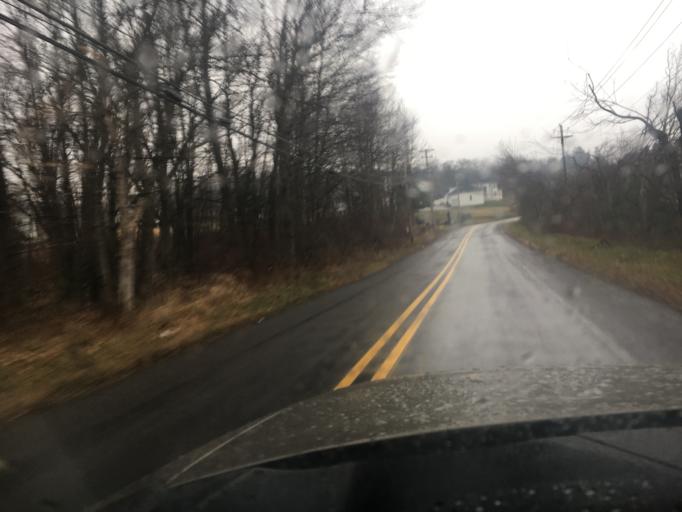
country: US
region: Pennsylvania
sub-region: Luzerne County
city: Harleigh
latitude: 41.0356
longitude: -75.9736
